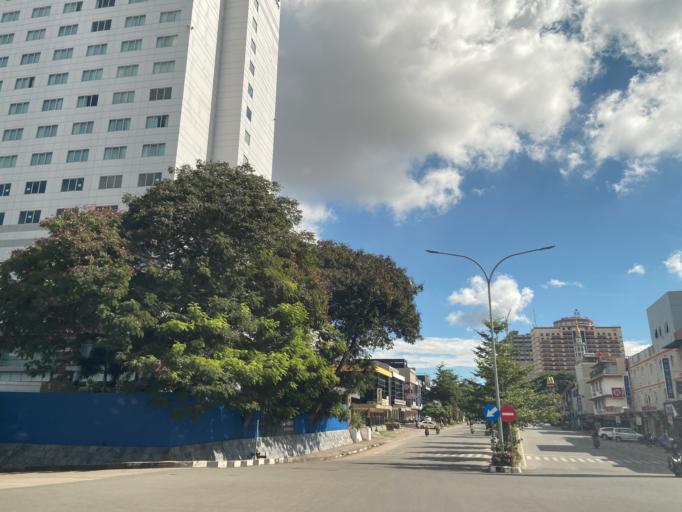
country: SG
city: Singapore
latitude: 1.1483
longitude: 104.0070
